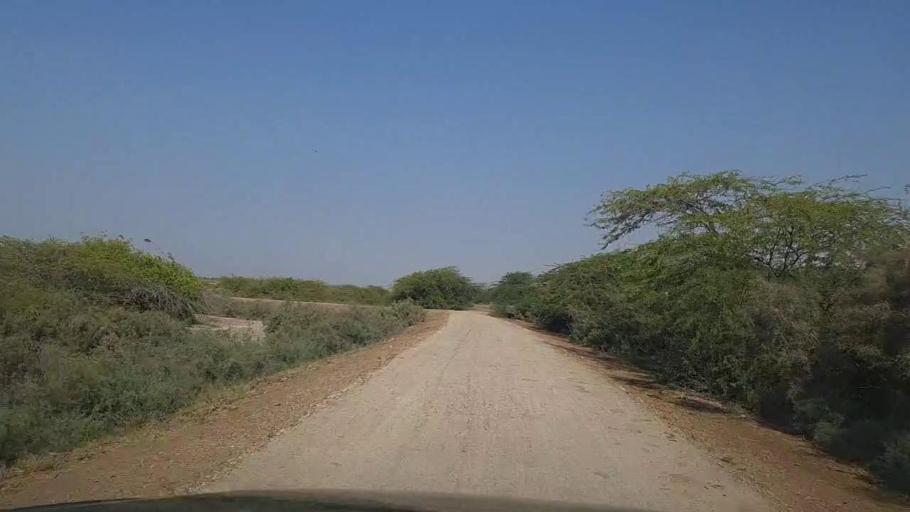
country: PK
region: Sindh
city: Thatta
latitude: 24.6487
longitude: 67.8170
